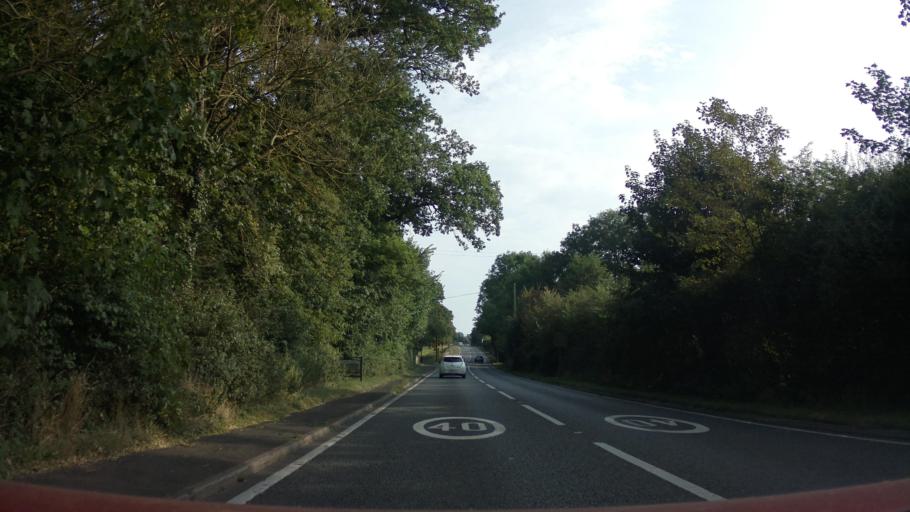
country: GB
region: England
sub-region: Warwickshire
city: Studley
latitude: 52.2457
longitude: -1.8851
